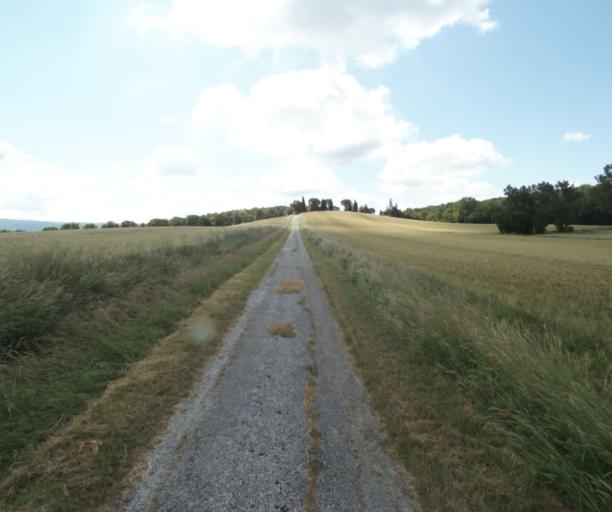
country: FR
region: Midi-Pyrenees
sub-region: Departement de la Haute-Garonne
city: Saint-Felix-Lauragais
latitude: 43.4280
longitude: 1.9297
